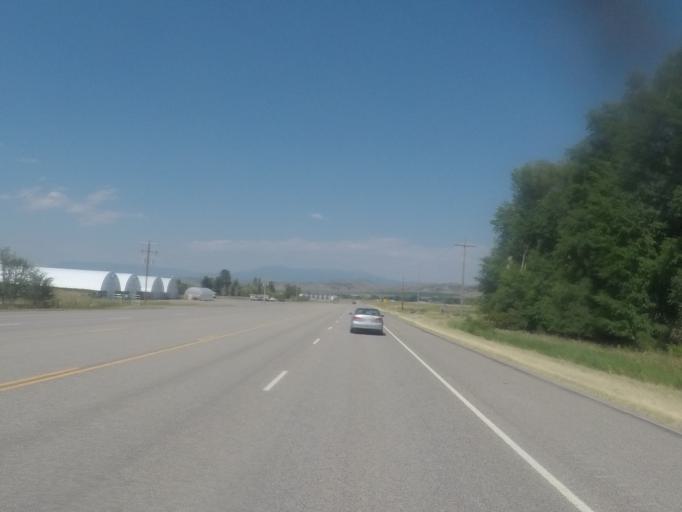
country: US
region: Montana
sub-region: Broadwater County
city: Townsend
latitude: 46.1568
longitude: -111.4613
